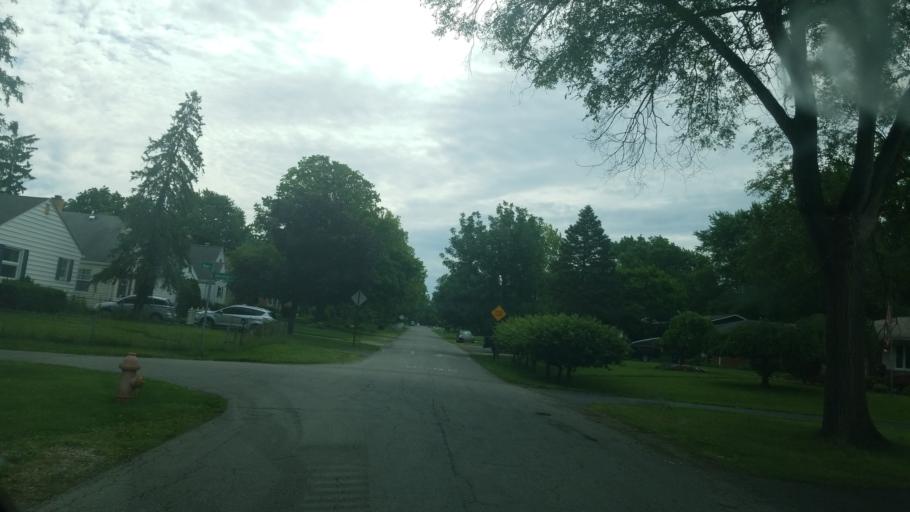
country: US
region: Ohio
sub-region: Franklin County
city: Worthington
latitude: 40.0744
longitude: -83.0148
